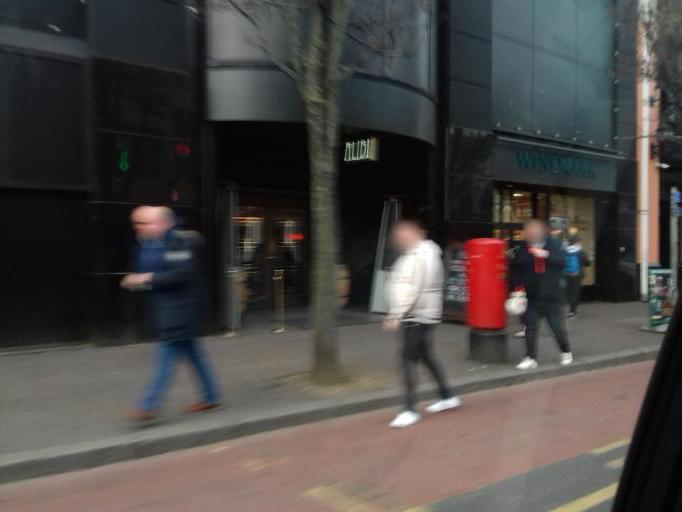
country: GB
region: Northern Ireland
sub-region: City of Belfast
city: Belfast
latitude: 54.5887
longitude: -5.9350
